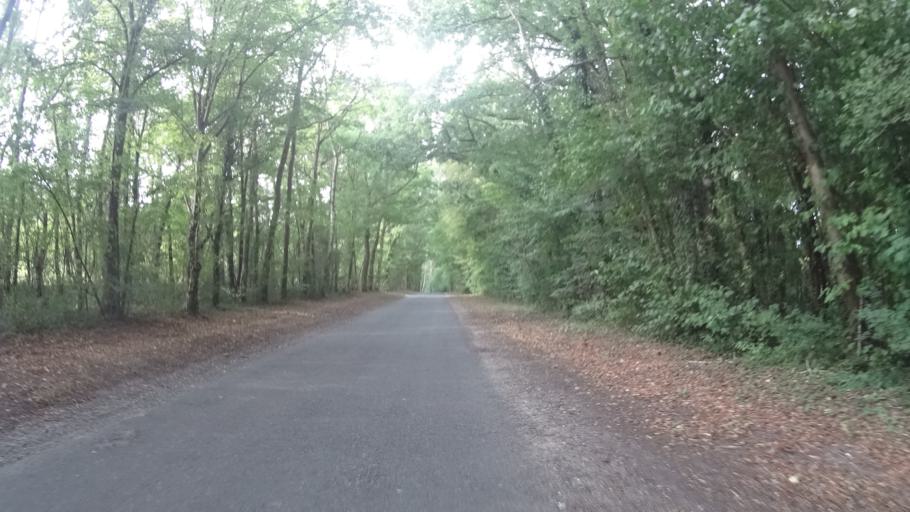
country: FR
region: Picardie
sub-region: Departement de l'Oise
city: Ver-sur-Launette
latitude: 49.1682
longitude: 2.6801
